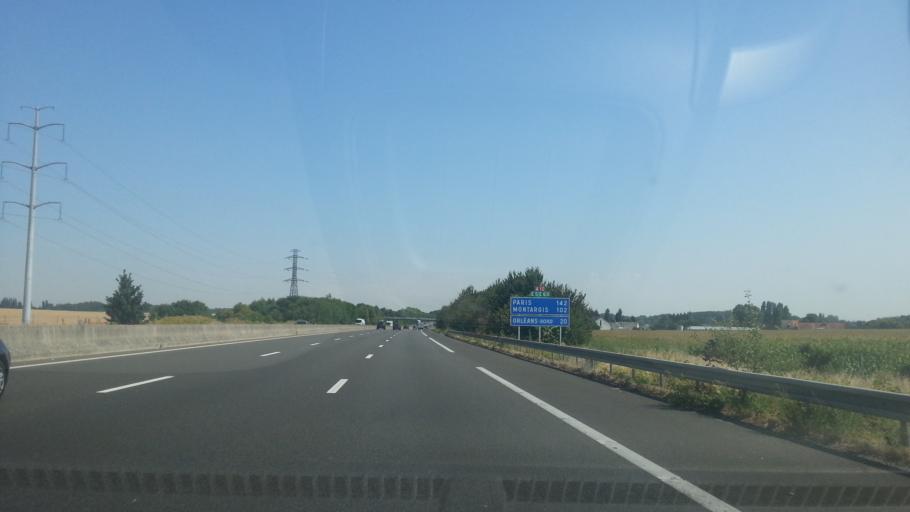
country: FR
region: Centre
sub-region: Departement du Loiret
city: Meung-sur-Loire
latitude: 47.8435
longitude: 1.6781
